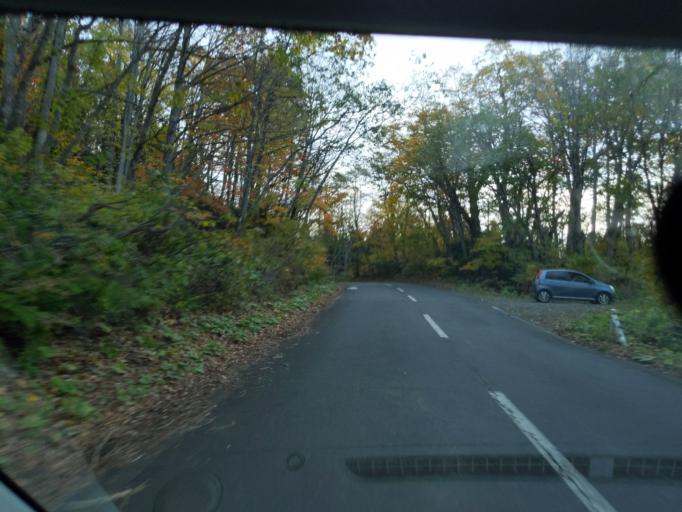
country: JP
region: Iwate
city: Mizusawa
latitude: 39.1074
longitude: 140.8734
